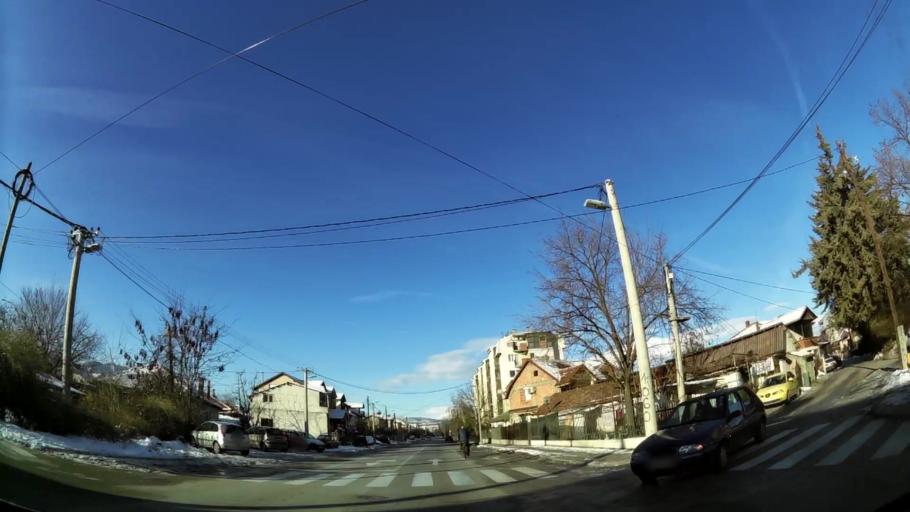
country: MK
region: Saraj
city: Saraj
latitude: 42.0087
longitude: 21.3479
